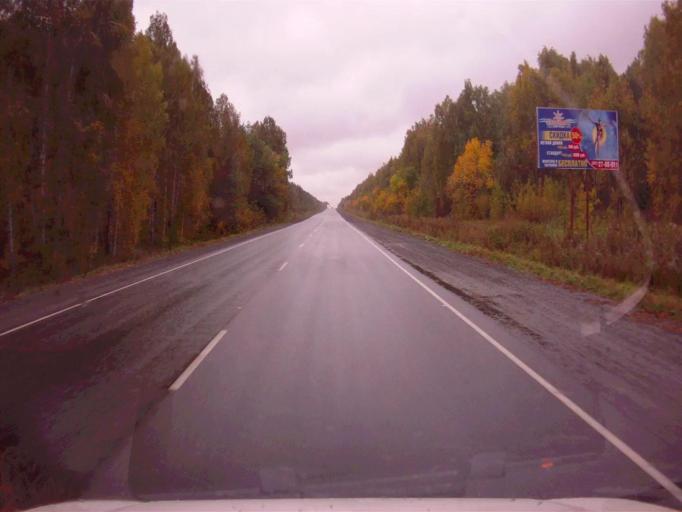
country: RU
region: Chelyabinsk
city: Roshchino
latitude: 55.3737
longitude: 61.1541
